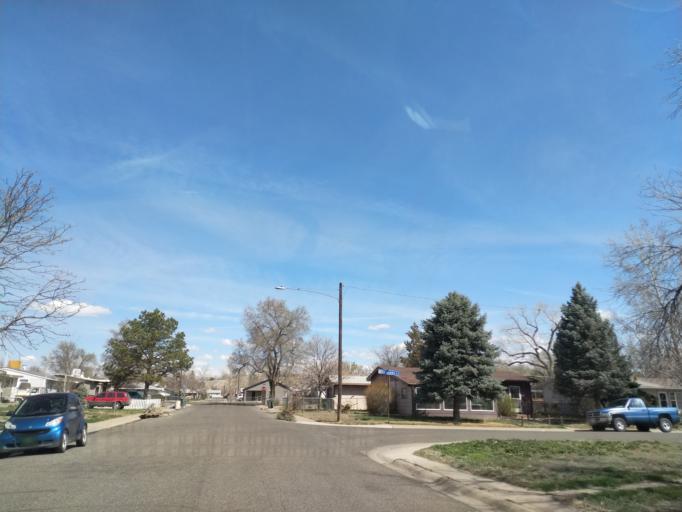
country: US
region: Colorado
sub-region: Mesa County
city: Grand Junction
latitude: 39.0801
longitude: -108.5361
